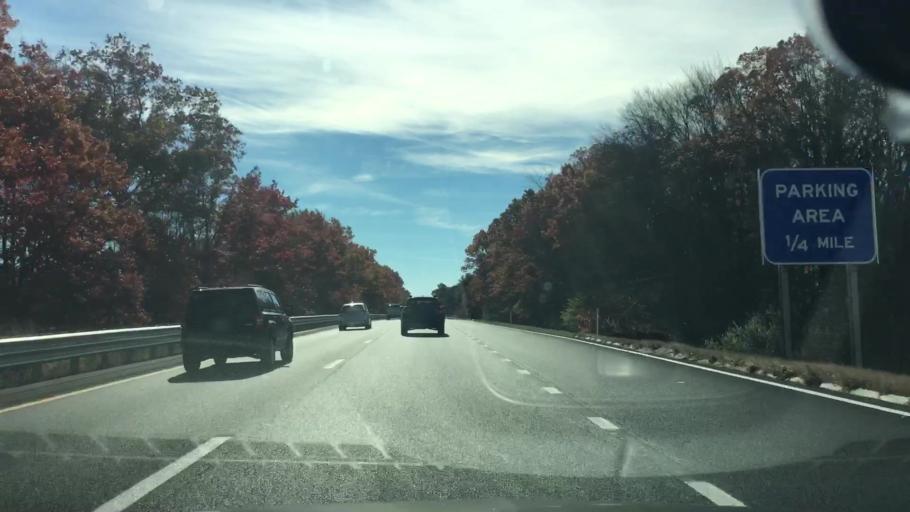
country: US
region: Massachusetts
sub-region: Franklin County
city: South Deerfield
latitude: 42.4620
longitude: -72.6169
